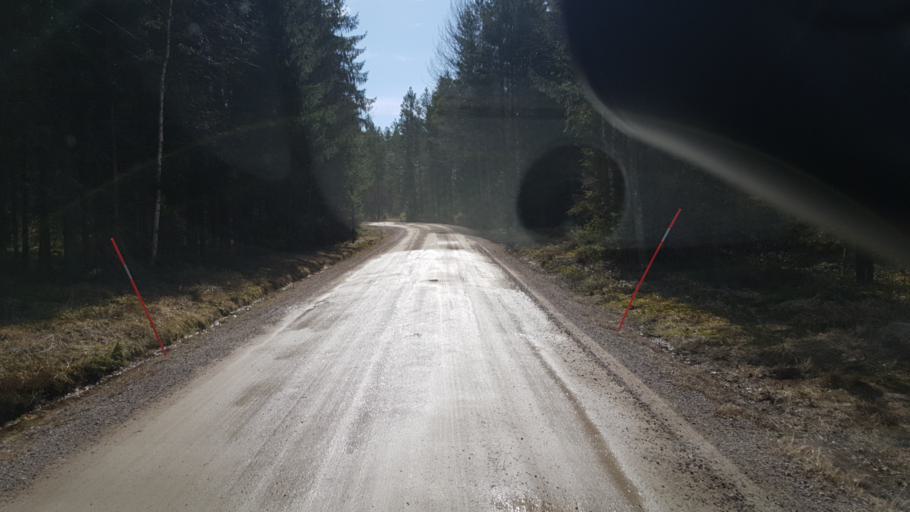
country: SE
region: Vaermland
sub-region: Arvika Kommun
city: Arvika
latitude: 59.5207
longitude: 12.7336
